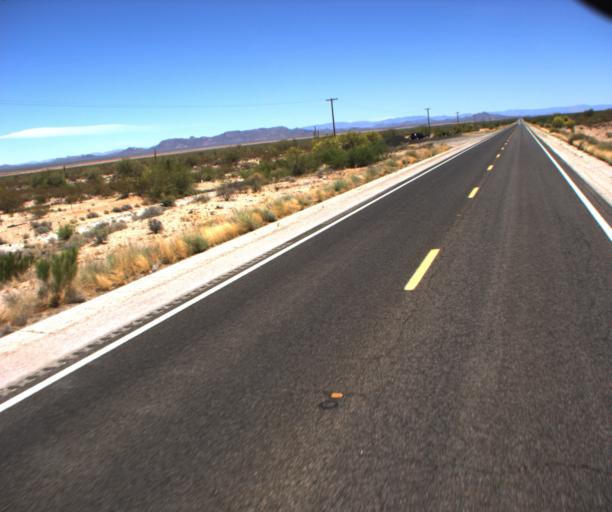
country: US
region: Arizona
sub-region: La Paz County
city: Salome
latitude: 33.9099
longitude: -113.2784
